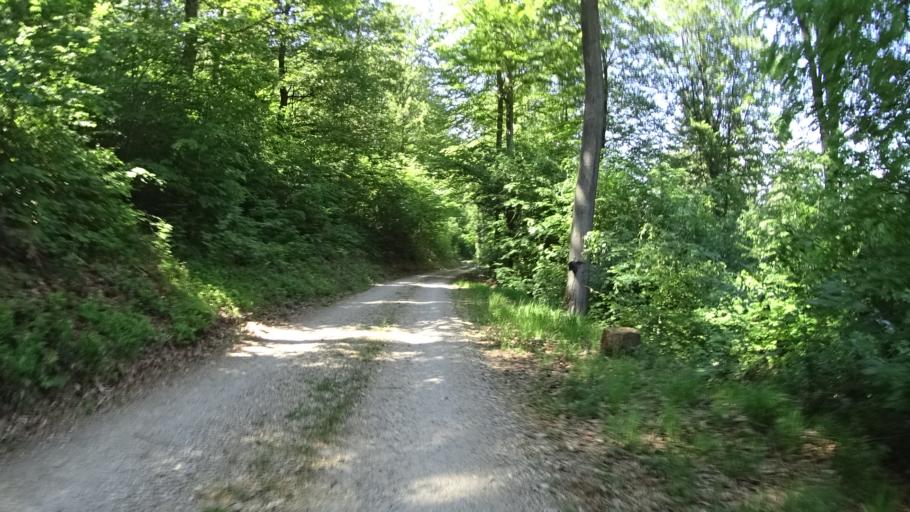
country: DE
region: Baden-Wuerttemberg
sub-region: Karlsruhe Region
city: Dossenheim
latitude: 49.4642
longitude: 8.7088
